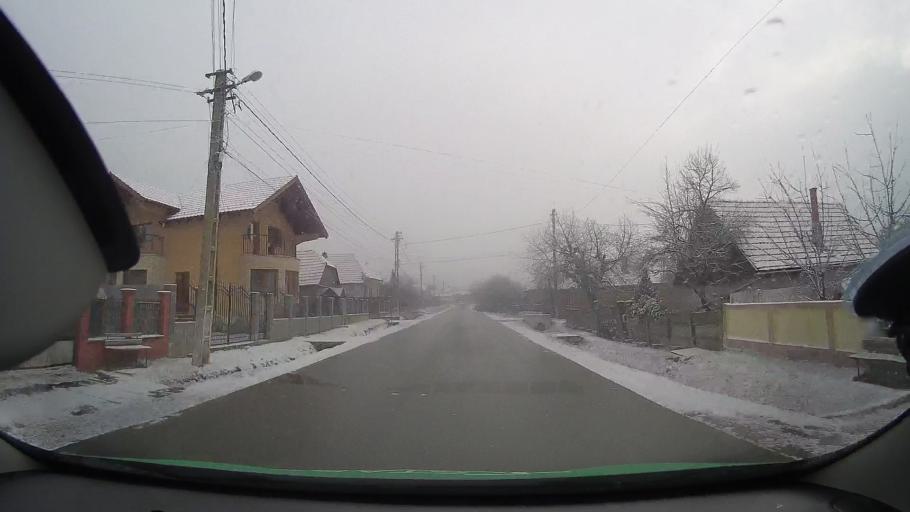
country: RO
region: Alba
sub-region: Municipiul Aiud
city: Ciumbrud
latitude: 46.3130
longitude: 23.7848
